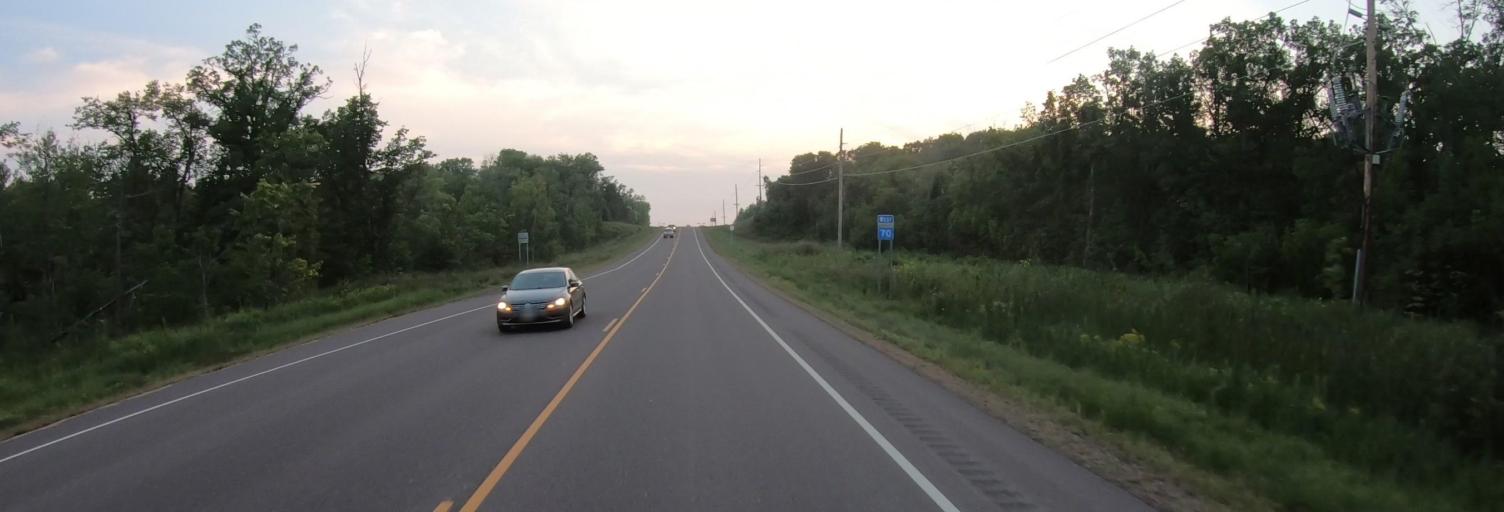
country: US
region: Wisconsin
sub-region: Burnett County
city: Grantsburg
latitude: 45.7734
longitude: -92.7839
